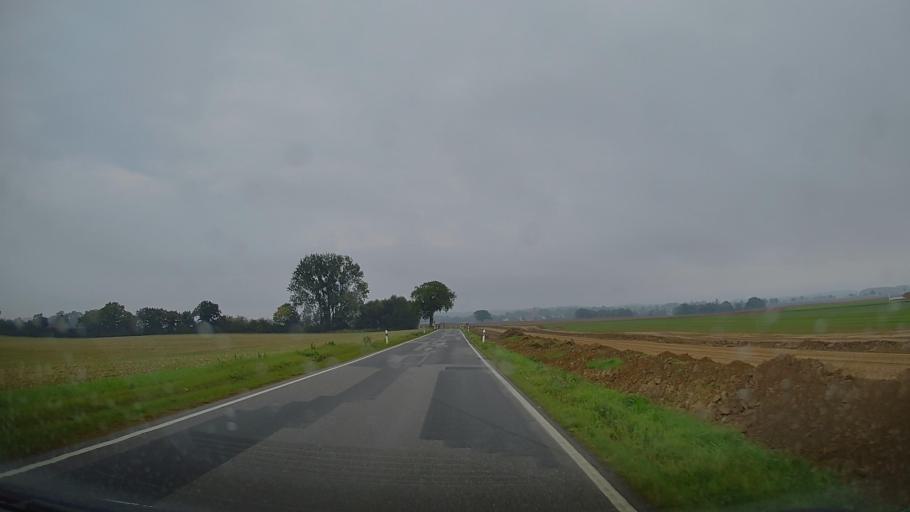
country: DE
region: Mecklenburg-Vorpommern
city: Kalkhorst
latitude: 53.9779
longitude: 11.0230
